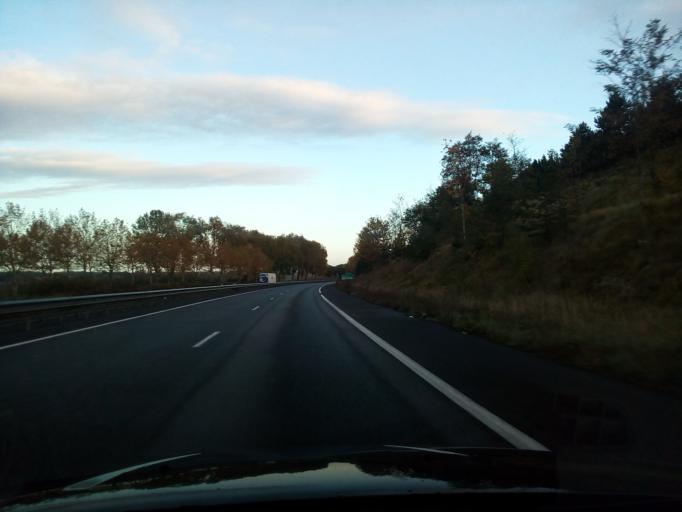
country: FR
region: Poitou-Charentes
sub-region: Departement de la Charente
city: Barbezieux-Saint-Hilaire
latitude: 45.4357
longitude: -0.1737
